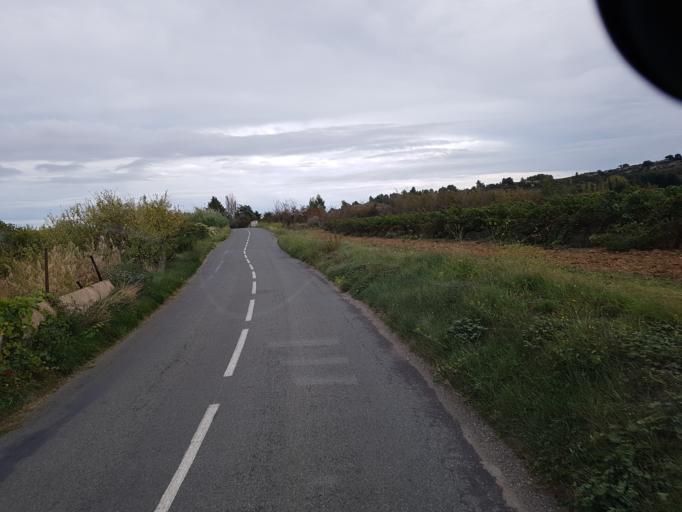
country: FR
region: Languedoc-Roussillon
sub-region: Departement de l'Aude
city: Narbonne
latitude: 43.1369
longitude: 2.9815
